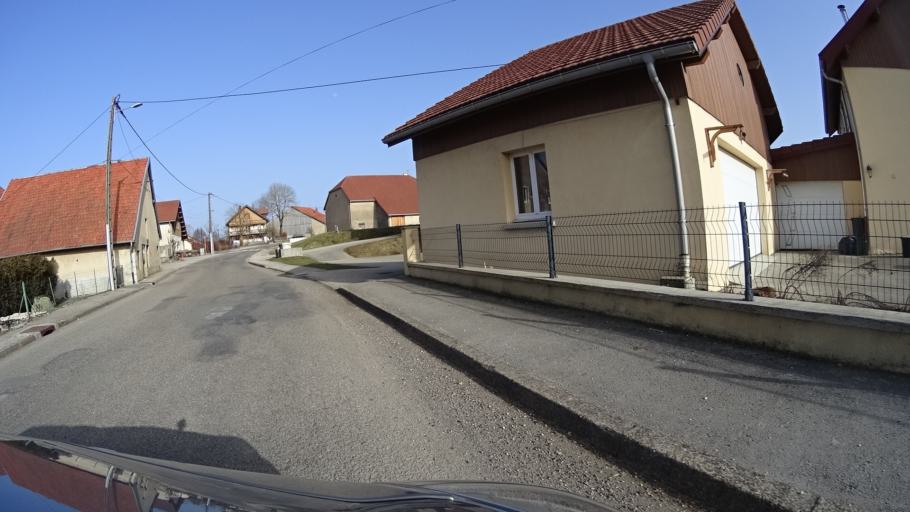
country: FR
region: Franche-Comte
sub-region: Departement du Doubs
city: Frasne
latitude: 46.8656
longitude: 6.2194
